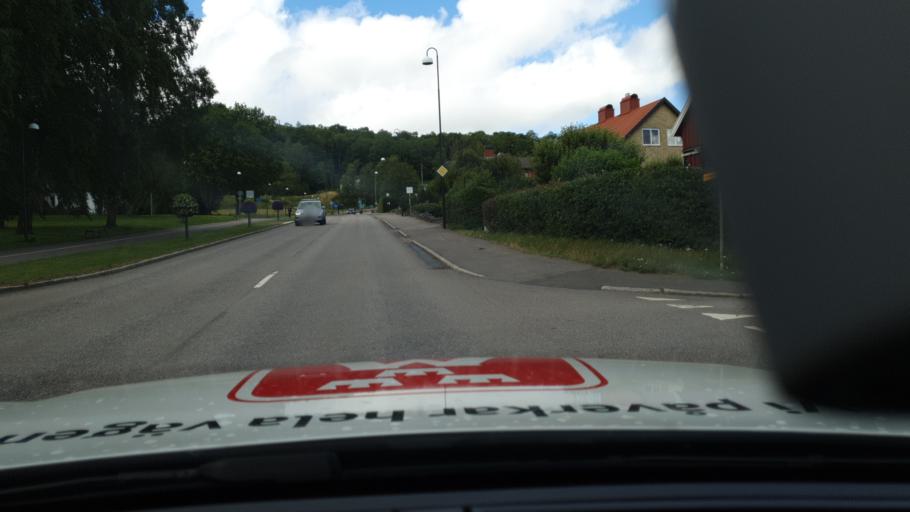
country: SE
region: Vaestra Goetaland
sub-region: Falkopings Kommun
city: Falkoeping
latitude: 58.1775
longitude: 13.5417
